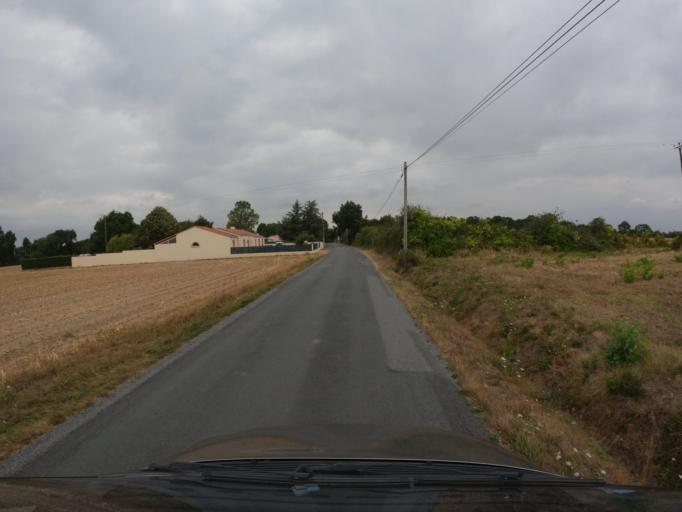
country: FR
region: Pays de la Loire
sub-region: Departement de la Vendee
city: La Guyonniere
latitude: 46.9675
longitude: -1.2712
